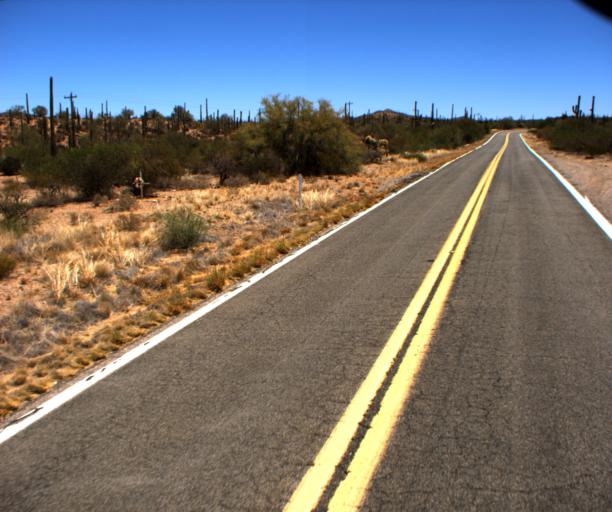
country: US
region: Arizona
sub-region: Pima County
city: Sells
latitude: 32.1728
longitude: -112.2052
